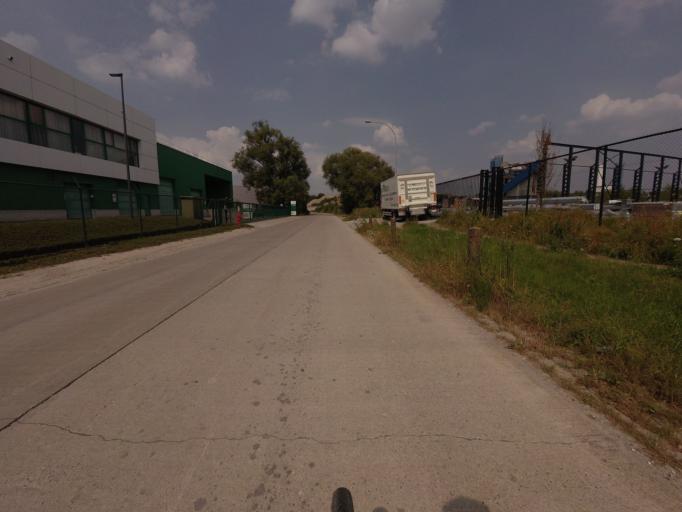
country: BE
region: Flanders
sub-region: Provincie Antwerpen
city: Schoten
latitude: 51.2357
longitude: 4.5013
